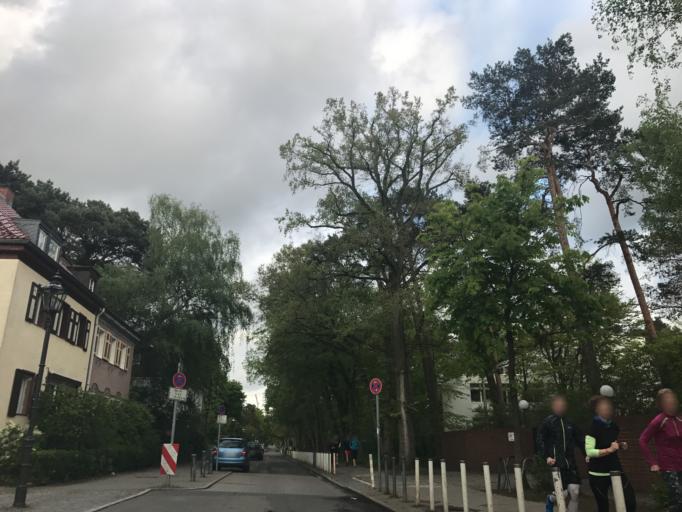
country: DE
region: Berlin
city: Grunewald
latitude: 52.5032
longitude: 13.2574
